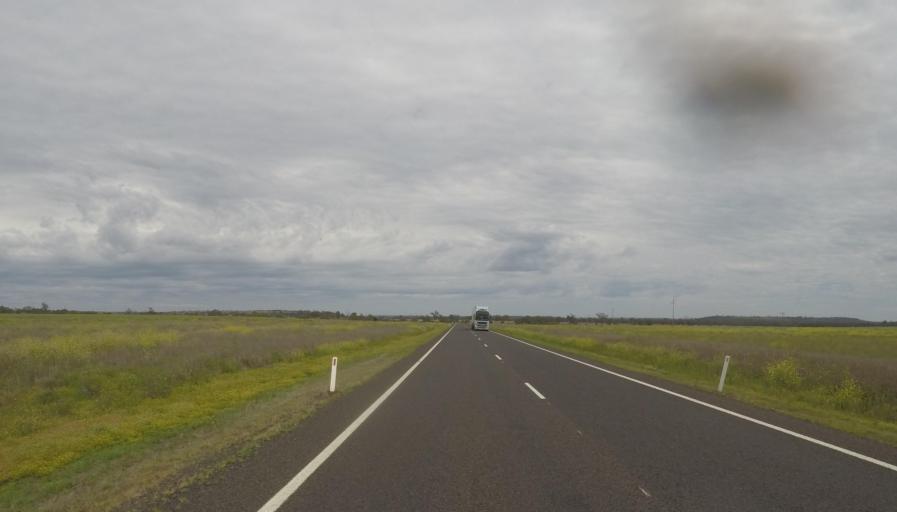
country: AU
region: Queensland
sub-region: Maranoa
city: Roma
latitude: -26.5374
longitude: 148.2339
